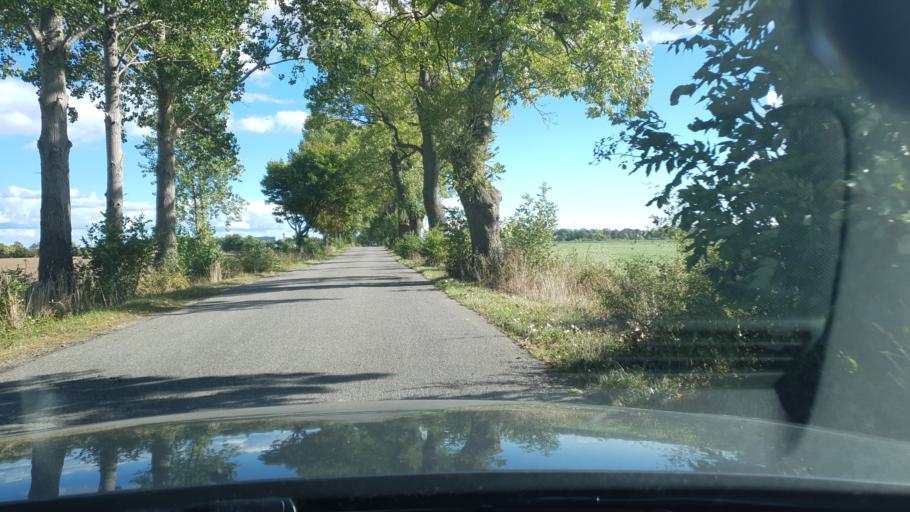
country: PL
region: Pomeranian Voivodeship
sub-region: Powiat pucki
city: Zelistrzewo
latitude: 54.6873
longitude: 18.4430
